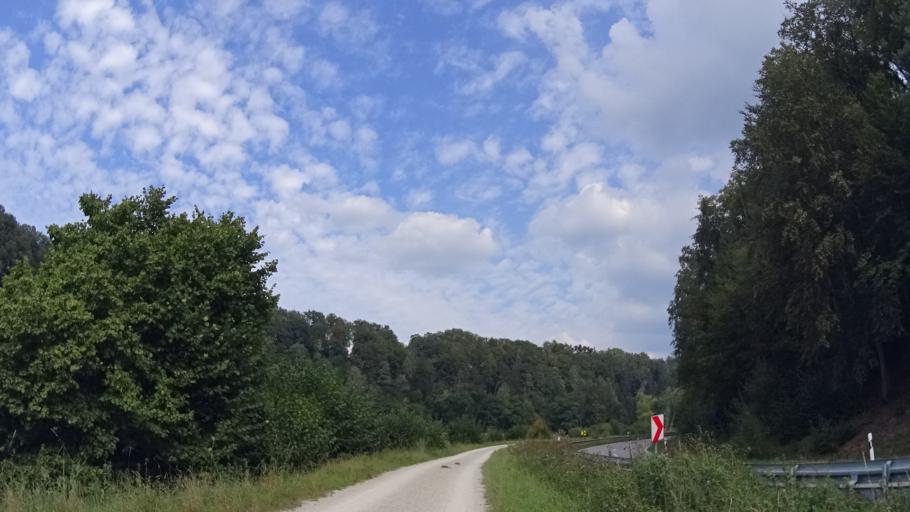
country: DE
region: Bavaria
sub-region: Lower Bavaria
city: Riedenburg
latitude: 48.9129
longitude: 11.6781
